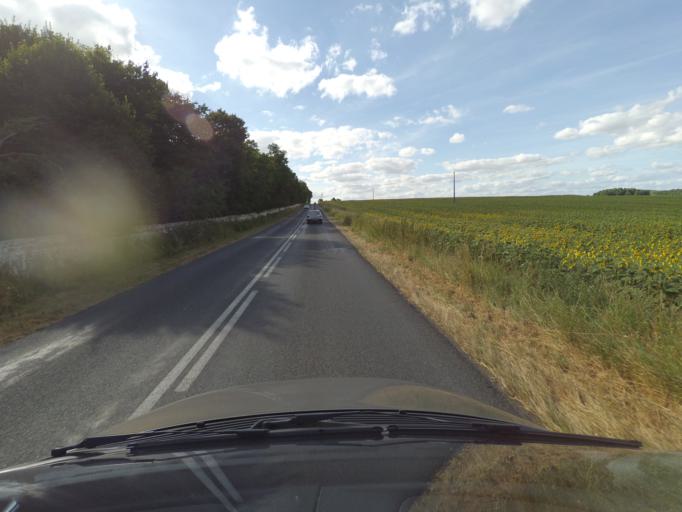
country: FR
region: Poitou-Charentes
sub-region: Departement de la Vienne
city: Saint-Gervais-les-Trois-Clochers
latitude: 46.9563
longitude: 0.3985
